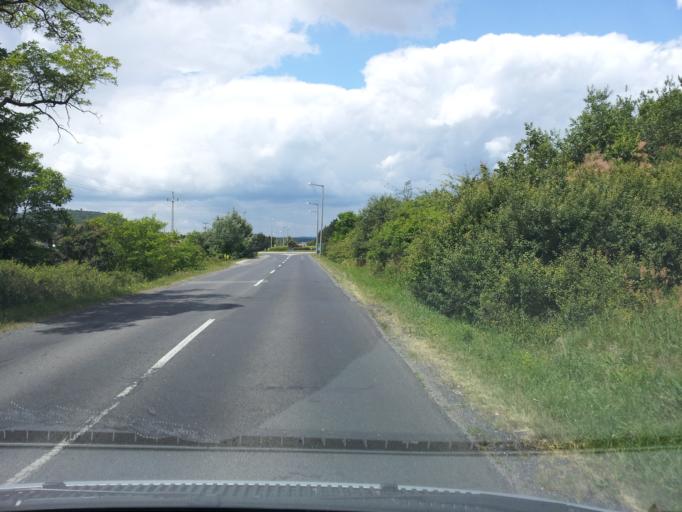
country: HU
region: Veszprem
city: Veszprem
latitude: 47.1069
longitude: 17.8709
